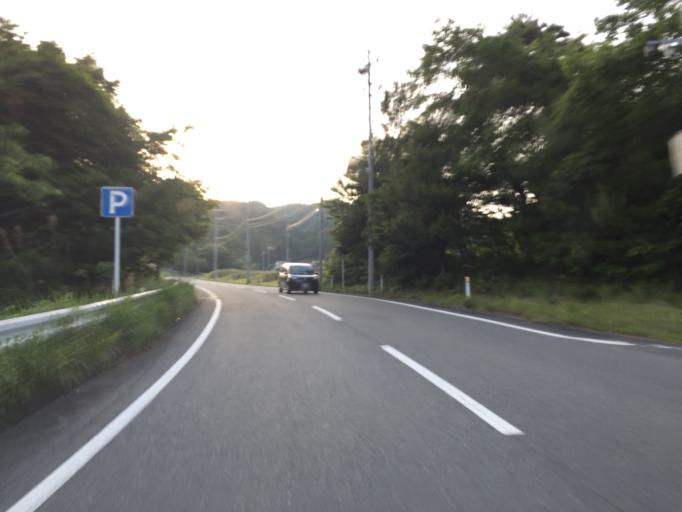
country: JP
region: Fukushima
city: Iwaki
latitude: 37.2431
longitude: 140.9689
